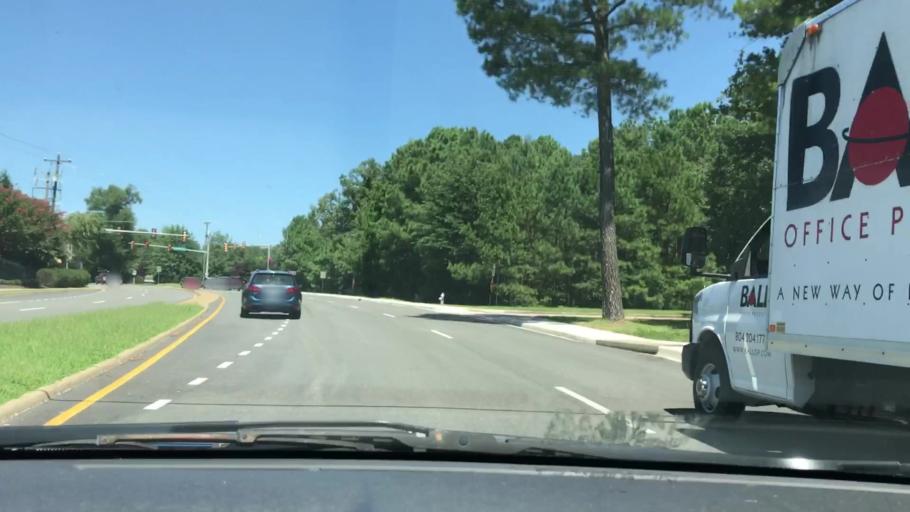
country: US
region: Virginia
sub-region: Henrico County
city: Short Pump
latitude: 37.6210
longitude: -77.6062
